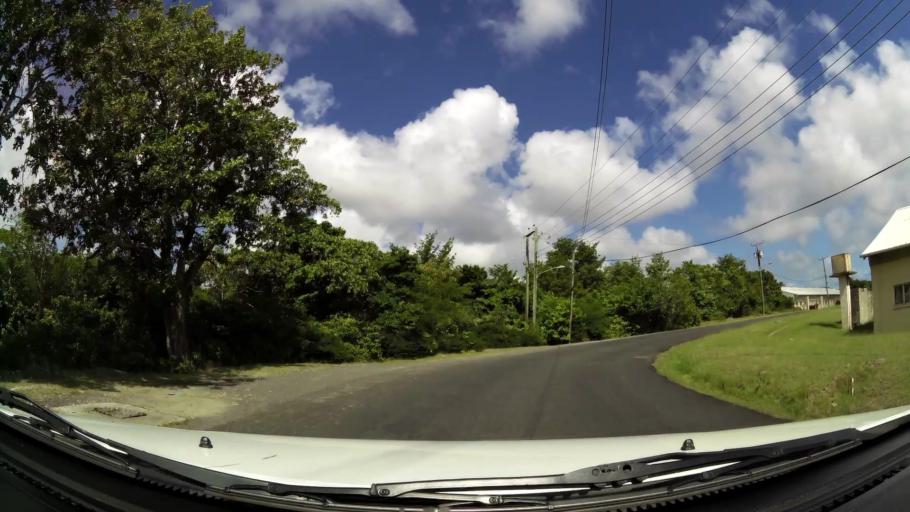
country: LC
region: Laborie Quarter
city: Laborie
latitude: 13.7419
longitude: -60.9725
